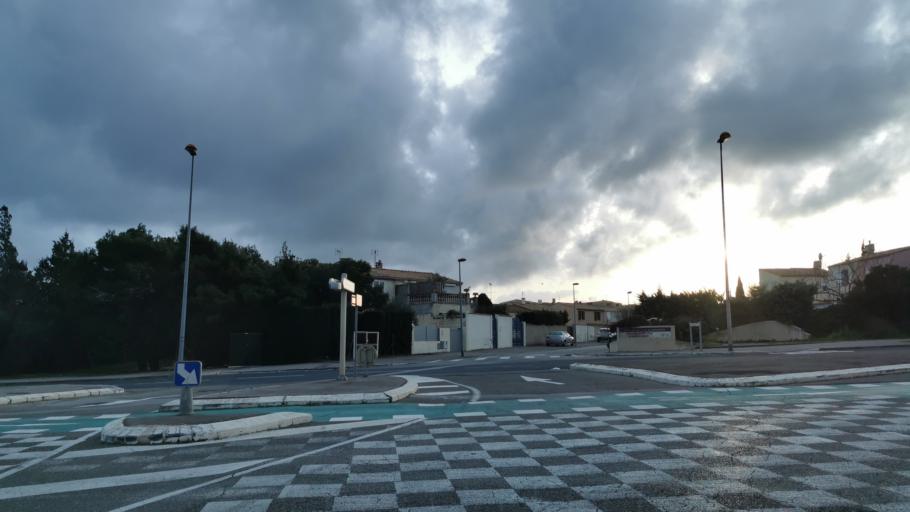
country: FR
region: Languedoc-Roussillon
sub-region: Departement de l'Aude
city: Narbonne
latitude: 43.1855
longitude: 2.9747
